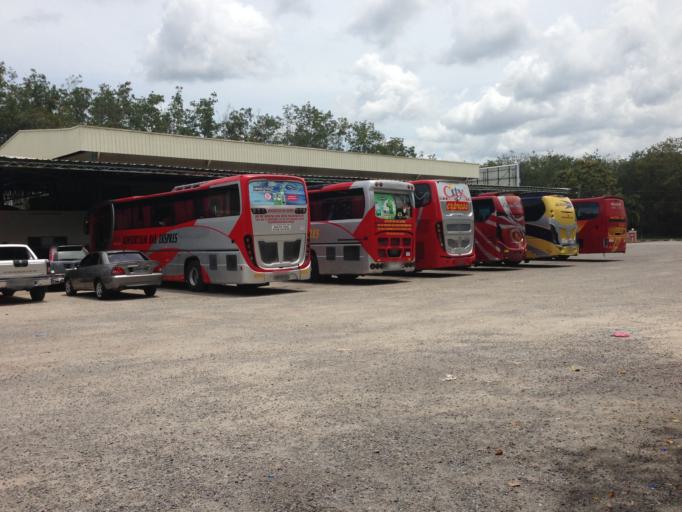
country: TH
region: Songkhla
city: Sadao
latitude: 6.4570
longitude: 100.4280
